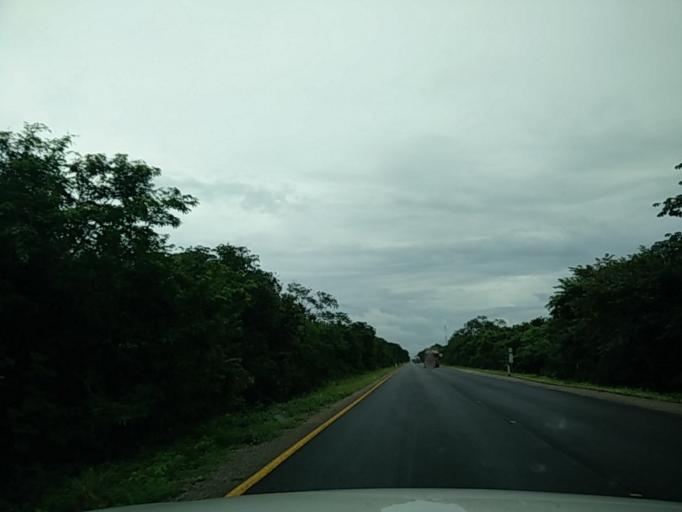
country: MX
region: Quintana Roo
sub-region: Lazaro Cardenas
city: Ignacio Zaragoza
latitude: 20.8859
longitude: -87.5588
